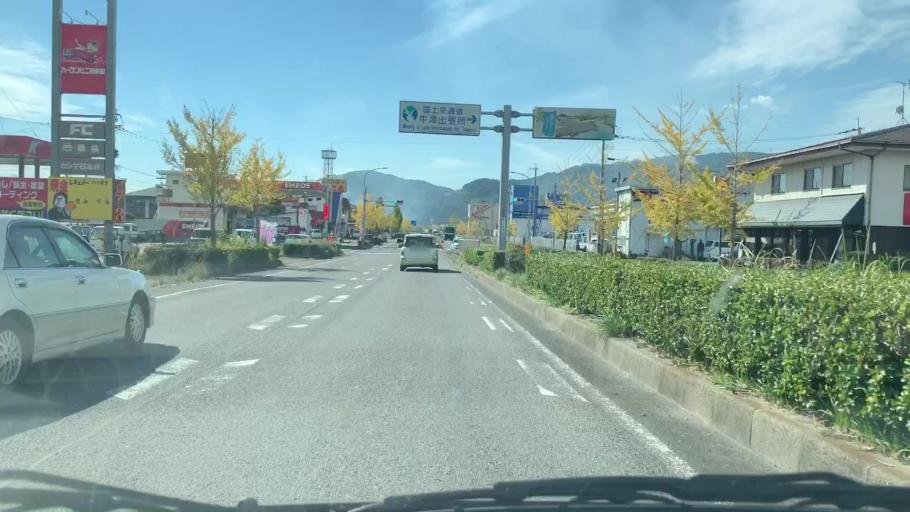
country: JP
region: Saga Prefecture
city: Saga-shi
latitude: 33.2461
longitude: 130.1909
